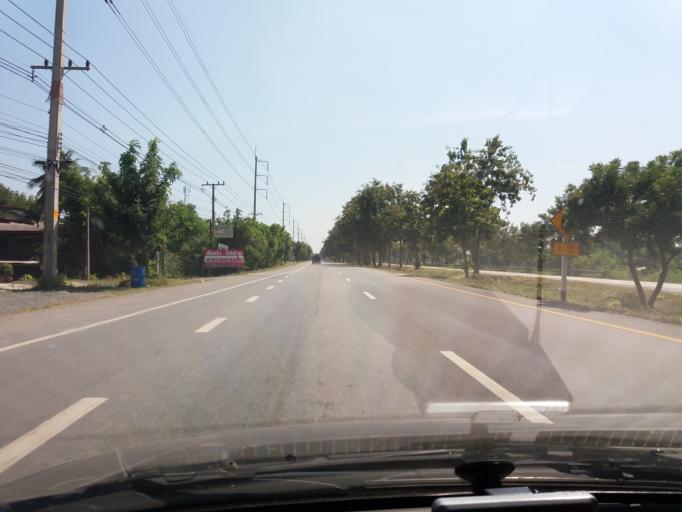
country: TH
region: Chai Nat
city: Sankhaburi
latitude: 15.0945
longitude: 100.1381
